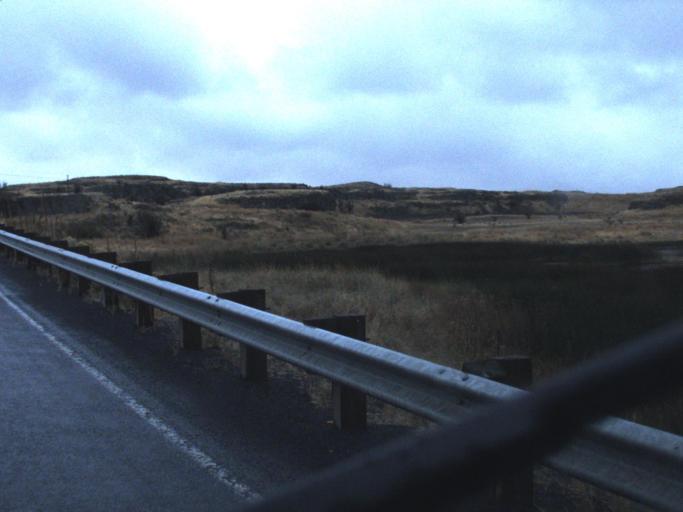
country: US
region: Washington
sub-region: Spokane County
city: Medical Lake
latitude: 47.2684
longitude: -117.9376
